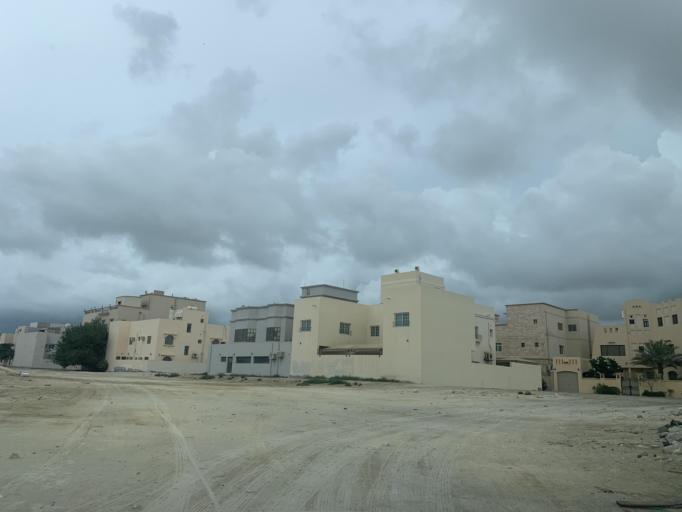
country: BH
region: Muharraq
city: Al Hadd
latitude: 26.2783
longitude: 50.6473
